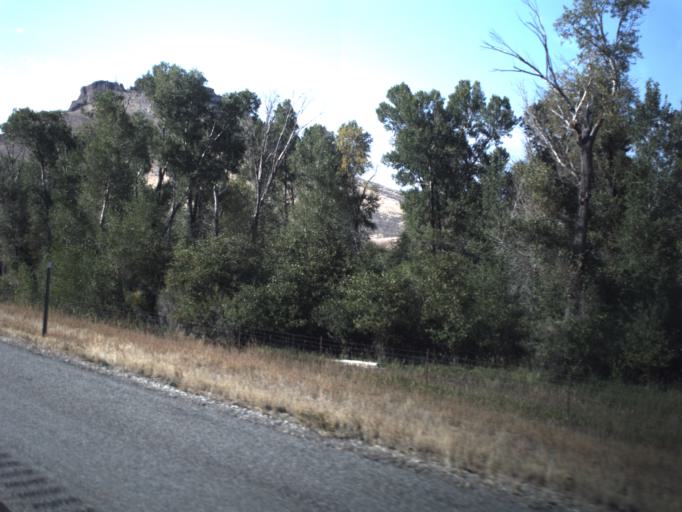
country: US
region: Utah
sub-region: Morgan County
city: Morgan
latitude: 41.0393
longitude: -111.5149
